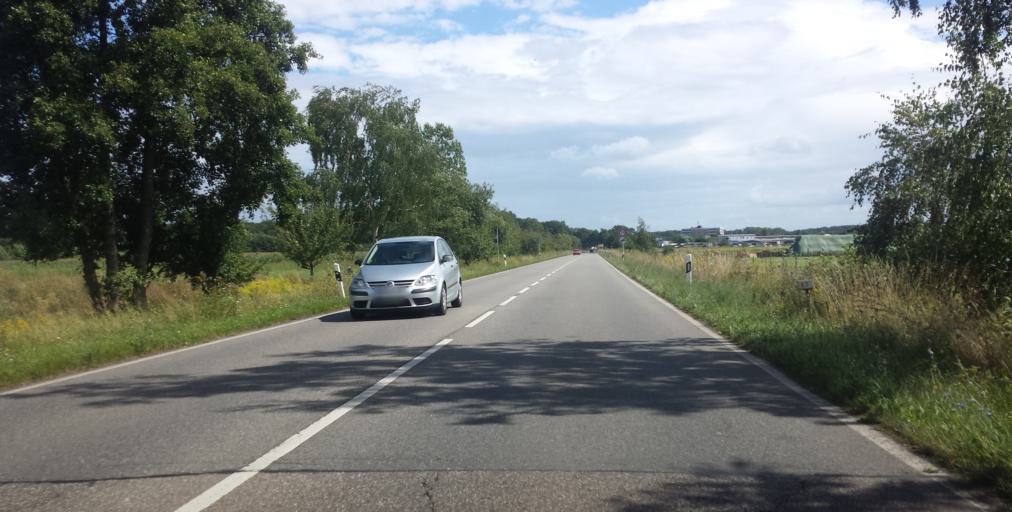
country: DE
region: Rheinland-Pfalz
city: Lachen-Speyerdorf
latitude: 49.3398
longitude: 8.2069
